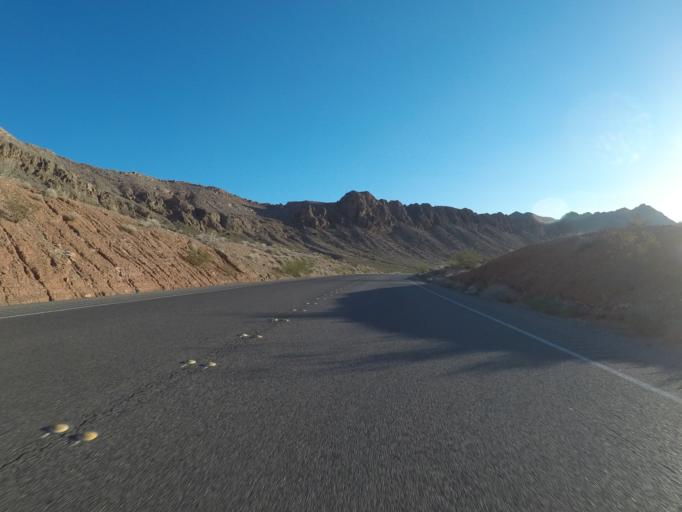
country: US
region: Nevada
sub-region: Clark County
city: Moapa Valley
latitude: 36.2557
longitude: -114.4819
